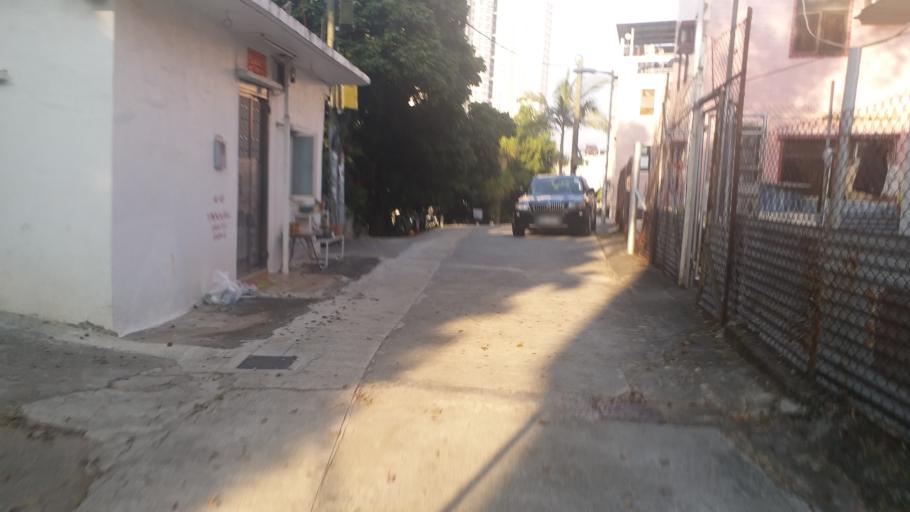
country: HK
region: Tuen Mun
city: Tuen Mun
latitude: 22.4121
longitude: 113.9746
